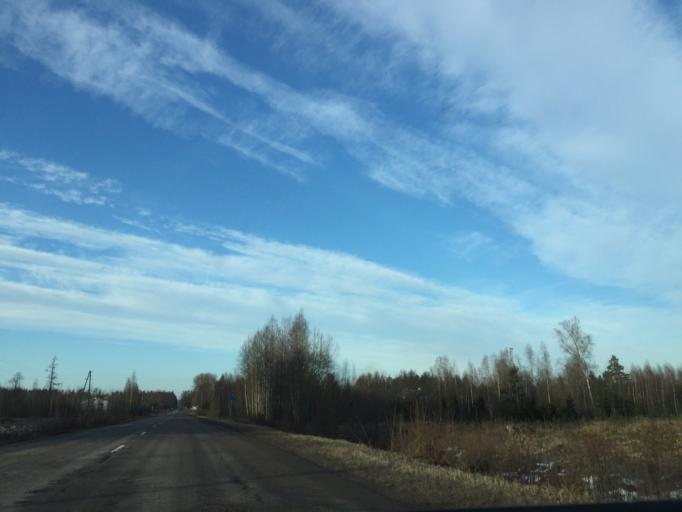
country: LV
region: Kekava
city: Balozi
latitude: 56.7298
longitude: 24.1100
